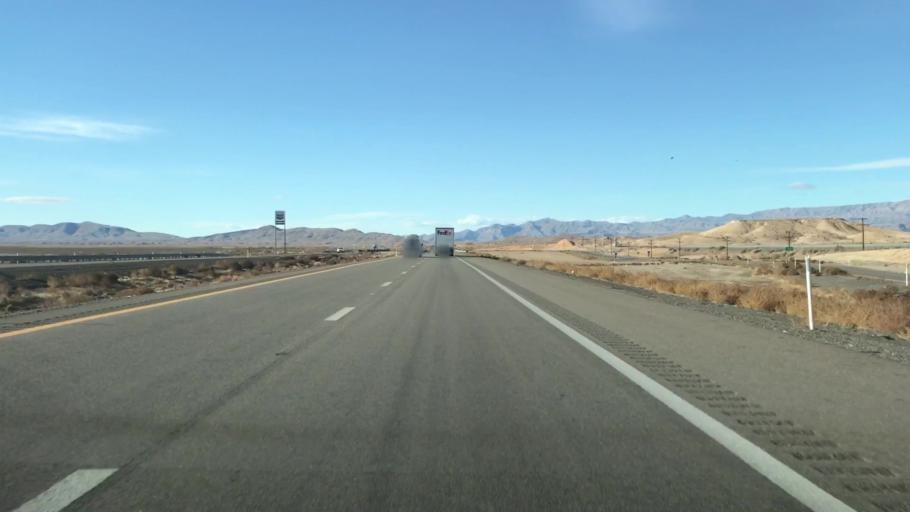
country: US
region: Nevada
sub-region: Clark County
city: Moapa Town
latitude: 36.5048
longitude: -114.7588
